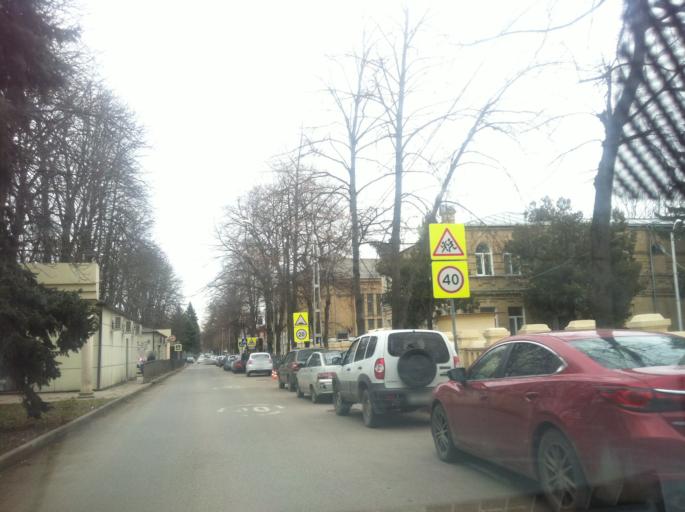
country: RU
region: Stavropol'skiy
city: Svobody
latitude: 44.0354
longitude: 43.0573
